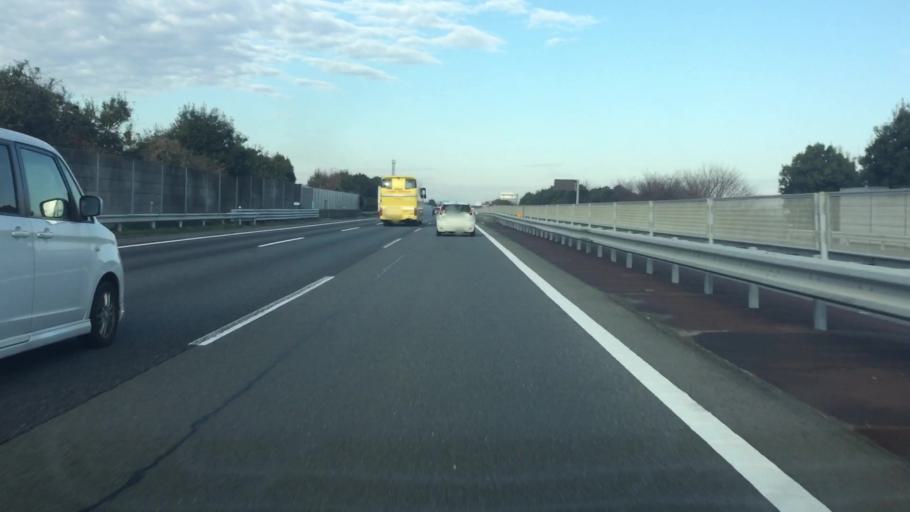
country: JP
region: Saitama
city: Yorii
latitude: 36.1268
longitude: 139.2441
